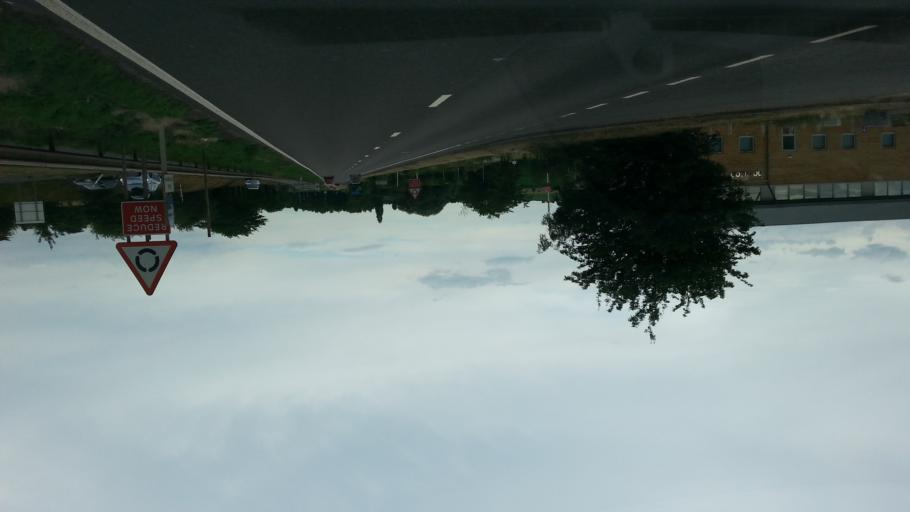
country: GB
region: England
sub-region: Herefordshire
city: Ross on Wye
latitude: 51.9281
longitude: -2.5690
